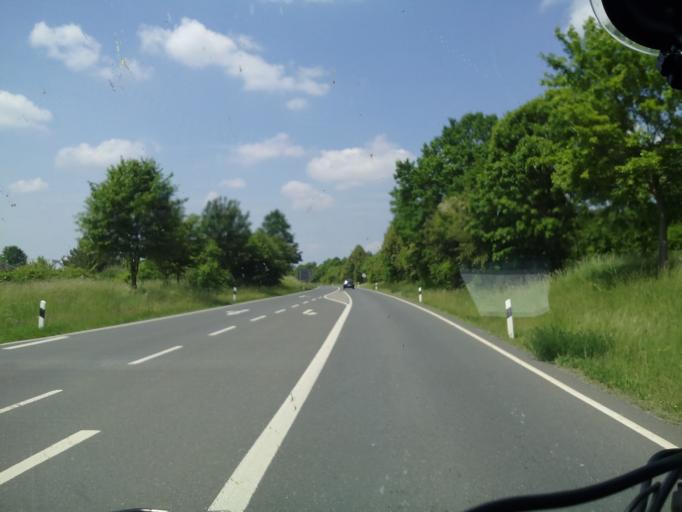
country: DE
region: Bavaria
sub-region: Upper Franconia
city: Mainleus
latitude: 50.1041
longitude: 11.3863
